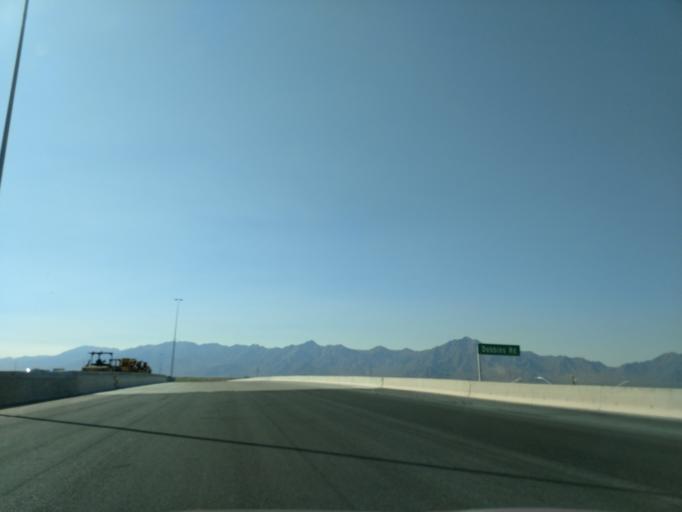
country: US
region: Arizona
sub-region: Maricopa County
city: Laveen
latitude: 33.3641
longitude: -112.1913
